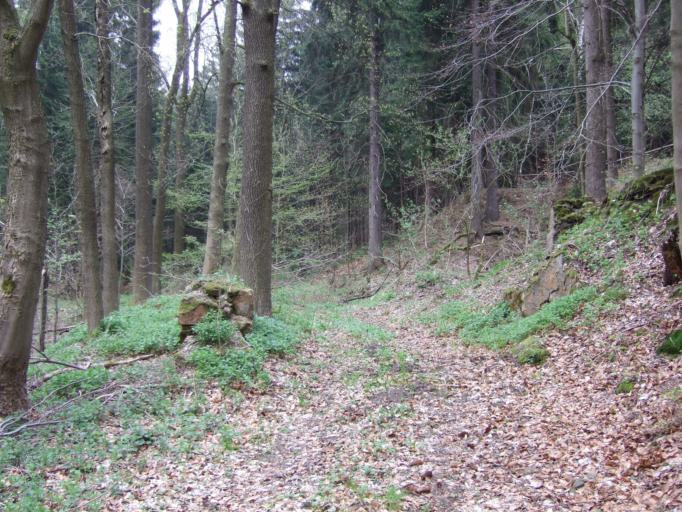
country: DE
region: Saxony
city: Rechenberg-Bienenmuhle
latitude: 50.7473
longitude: 13.5160
